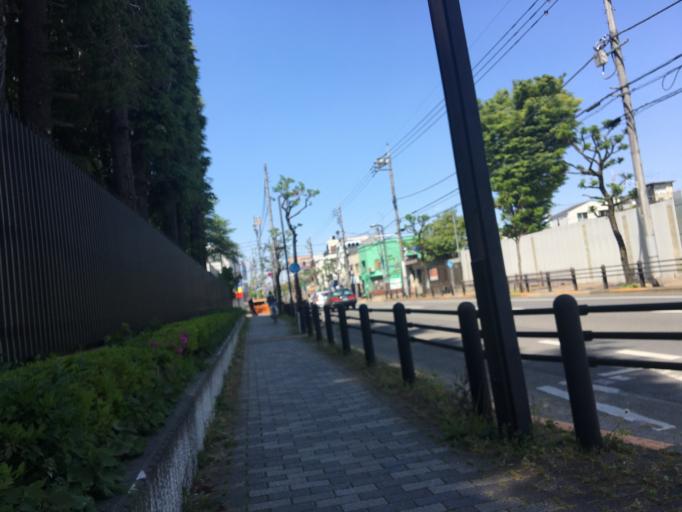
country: JP
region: Tokyo
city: Kokubunji
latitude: 35.7213
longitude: 139.4879
